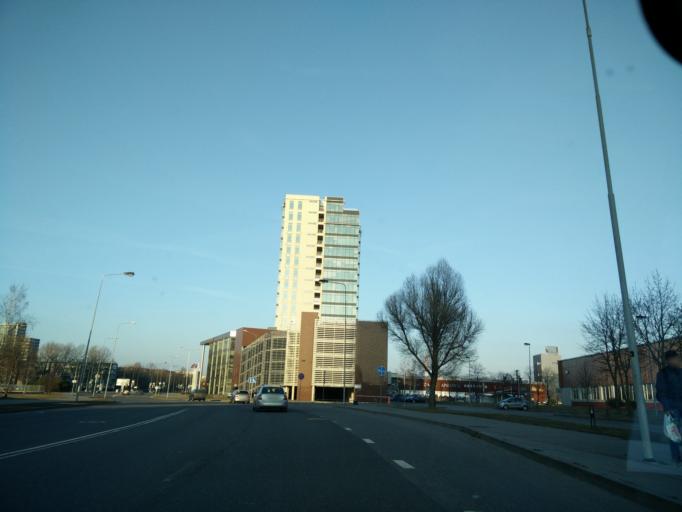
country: LT
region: Klaipedos apskritis
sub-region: Klaipeda
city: Klaipeda
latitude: 55.6916
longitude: 21.1495
